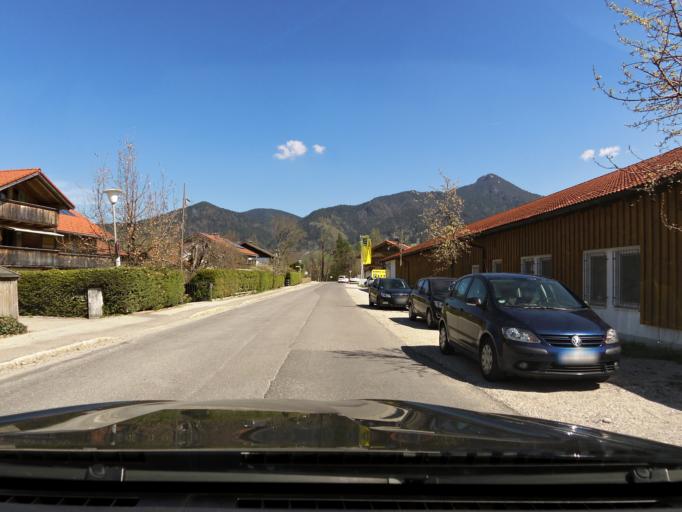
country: DE
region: Bavaria
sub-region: Upper Bavaria
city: Lenggries
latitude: 47.6804
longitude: 11.5675
